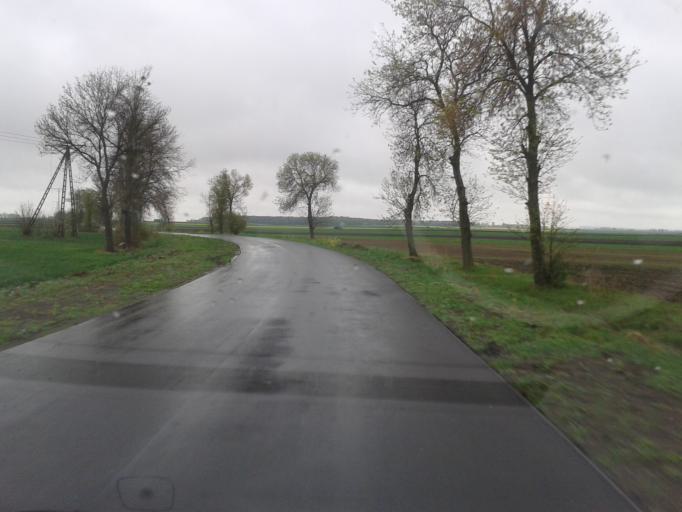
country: UA
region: Lviv
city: Uhniv
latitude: 50.4089
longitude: 23.7115
